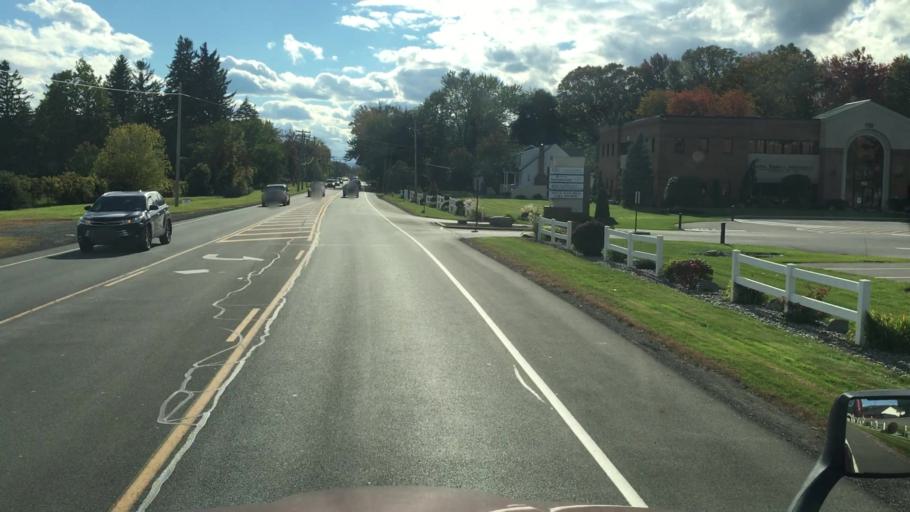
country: US
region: New York
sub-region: Schenectady County
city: East Glenville
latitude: 42.8589
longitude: -73.9361
